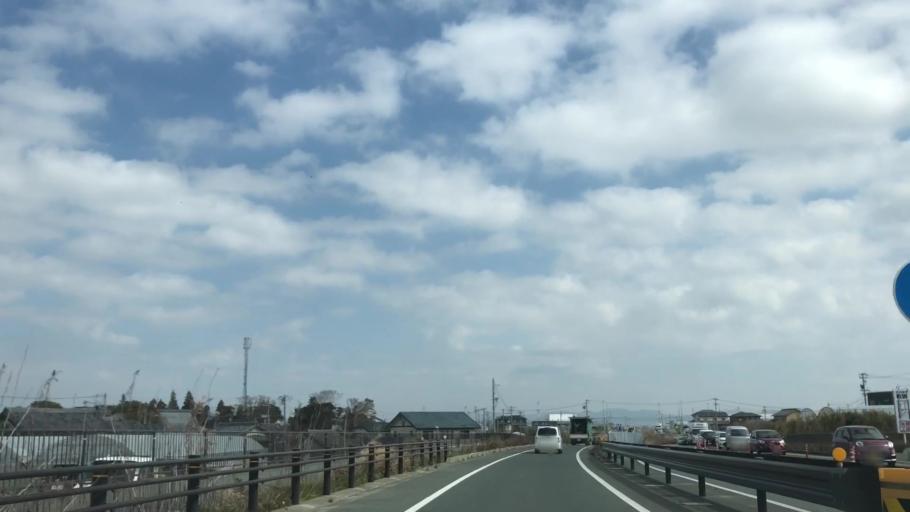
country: JP
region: Aichi
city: Tahara
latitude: 34.6976
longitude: 137.3350
